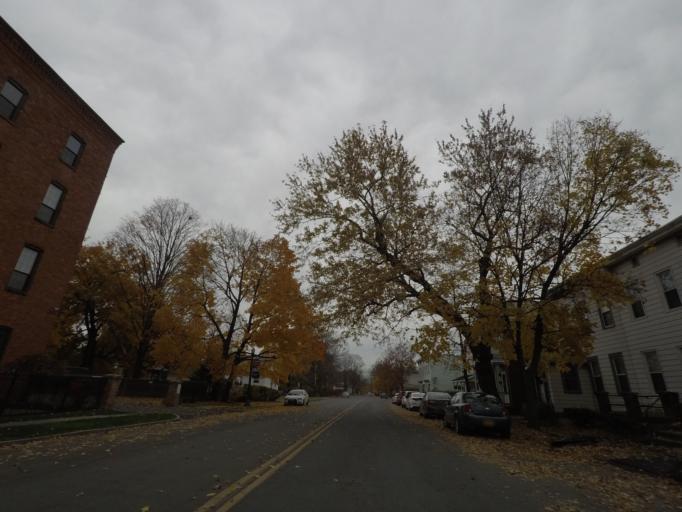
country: US
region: New York
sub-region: Albany County
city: Cohoes
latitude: 42.7676
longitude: -73.6792
